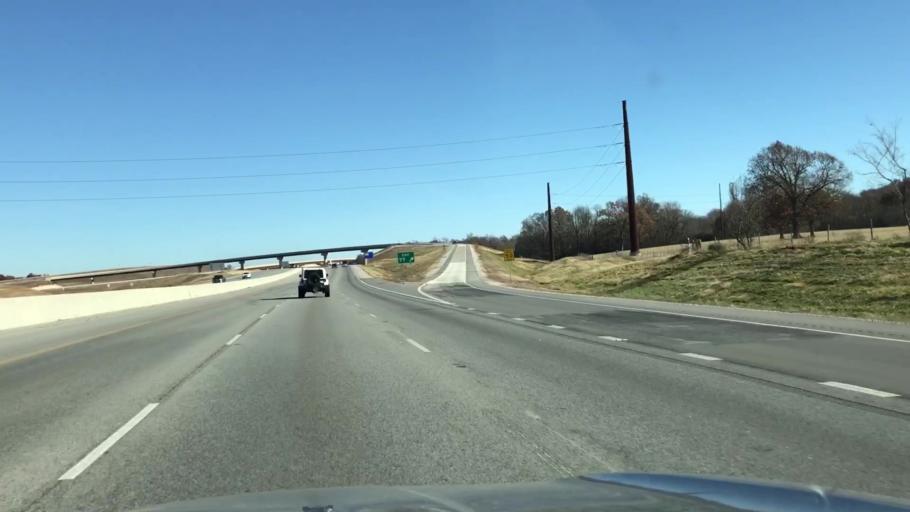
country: US
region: Arkansas
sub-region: Benton County
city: Lowell
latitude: 36.2346
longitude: -94.1679
